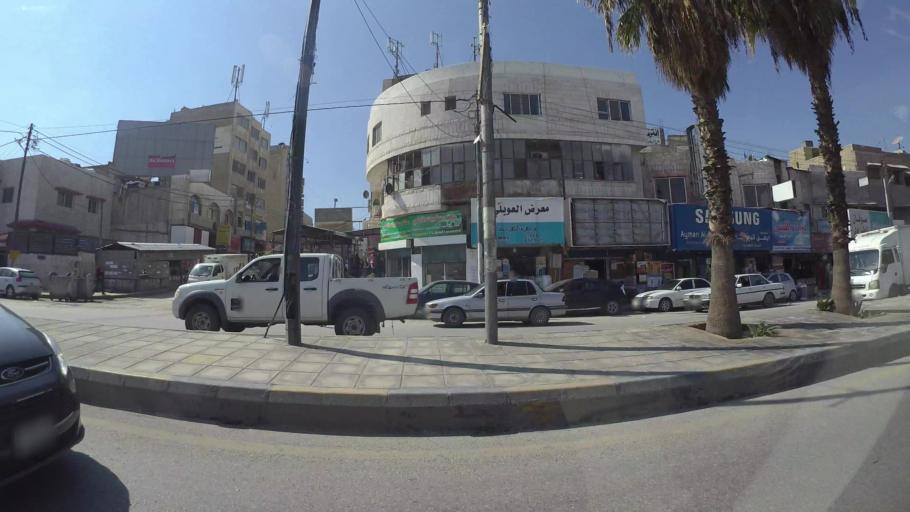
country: JO
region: Zarqa
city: Zarqa
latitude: 32.0628
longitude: 36.0946
